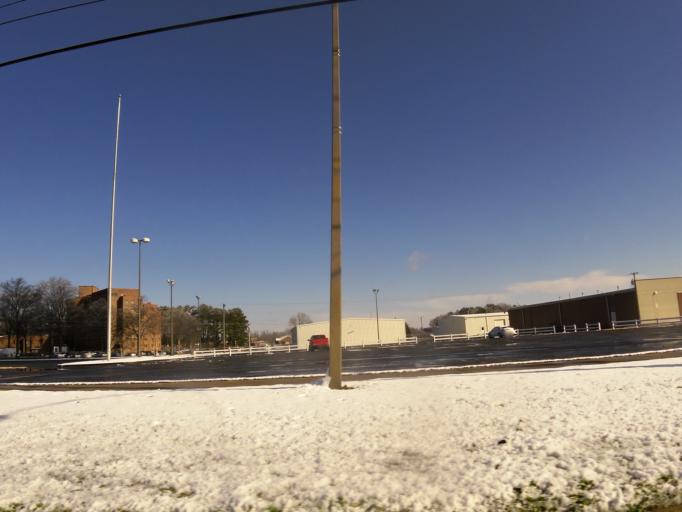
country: US
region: North Carolina
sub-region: Wilson County
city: Wilson
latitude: 35.7229
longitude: -77.8930
